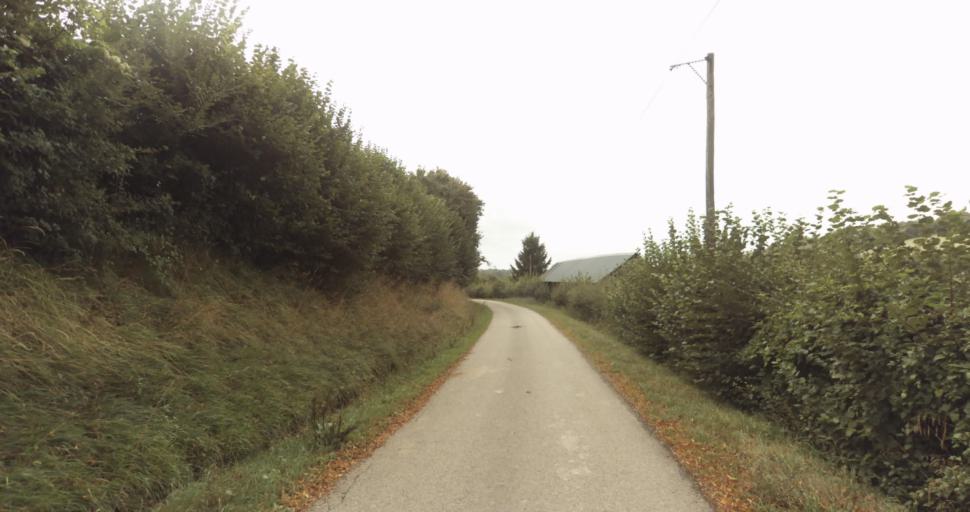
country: FR
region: Lower Normandy
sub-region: Departement de l'Orne
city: Gace
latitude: 48.8148
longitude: 0.3240
